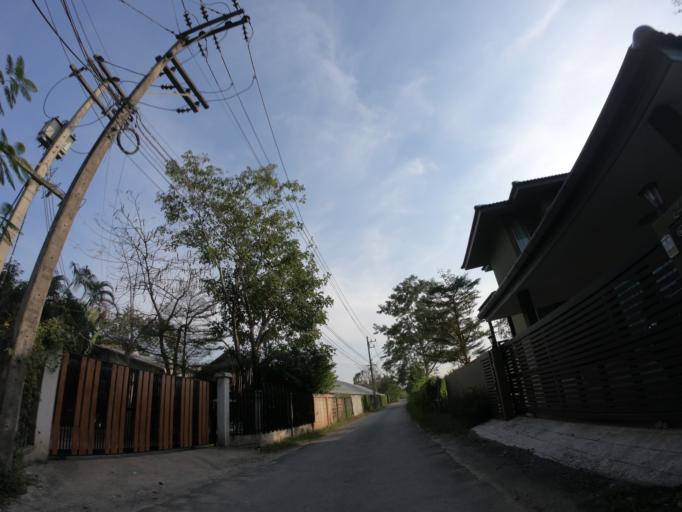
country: TH
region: Chiang Mai
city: Chiang Mai
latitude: 18.8326
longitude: 98.9818
